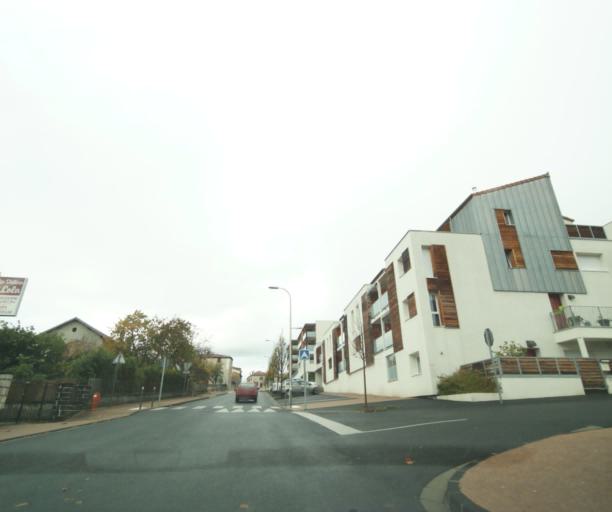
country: FR
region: Auvergne
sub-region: Departement du Puy-de-Dome
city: Cournon-d'Auvergne
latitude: 45.7399
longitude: 3.2023
